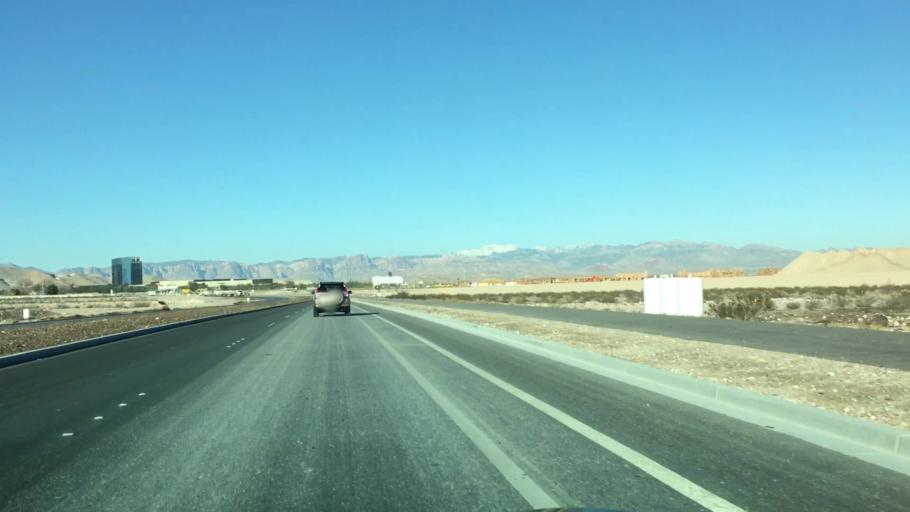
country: US
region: Nevada
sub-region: Clark County
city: Enterprise
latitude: 35.9614
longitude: -115.1533
